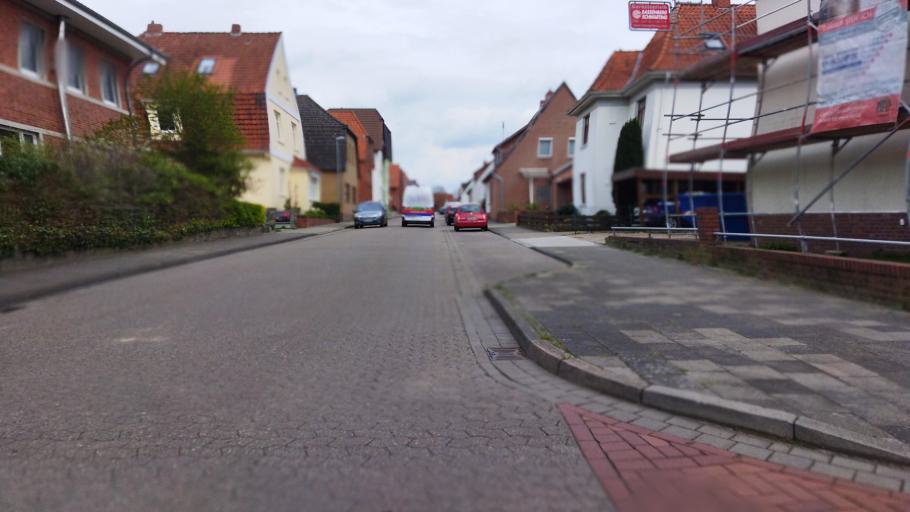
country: DE
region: Lower Saxony
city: Verden
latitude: 52.9278
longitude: 9.2267
